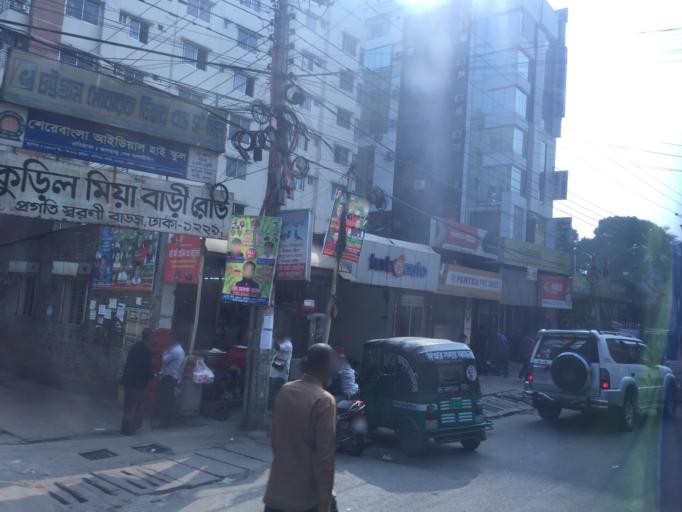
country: BD
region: Dhaka
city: Tungi
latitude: 23.8175
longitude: 90.4211
